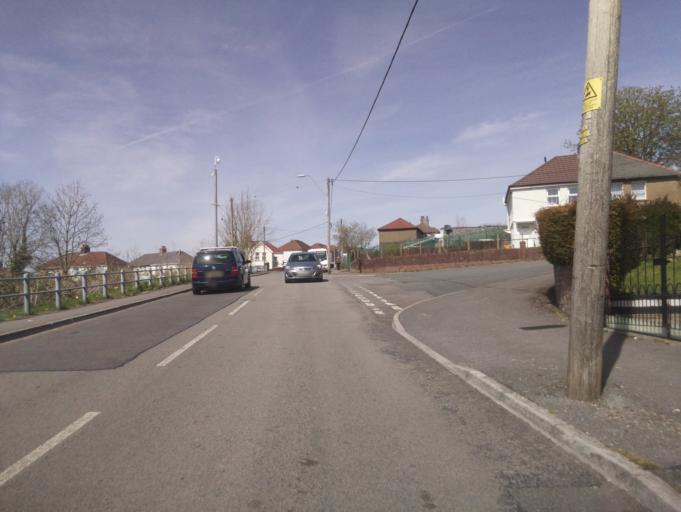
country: GB
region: Wales
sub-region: Merthyr Tydfil County Borough
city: Merthyr Tydfil
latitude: 51.7627
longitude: -3.3723
